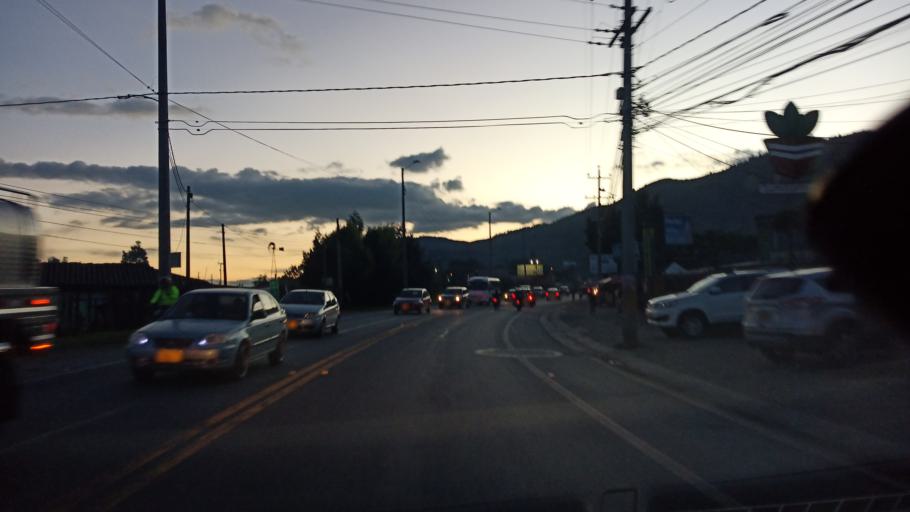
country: CO
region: Cundinamarca
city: Chia
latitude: 4.8501
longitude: -74.0738
